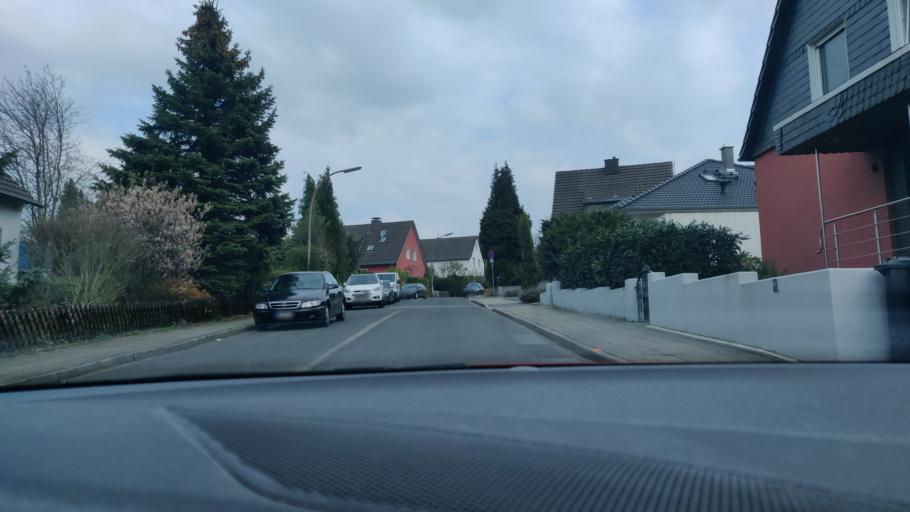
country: DE
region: North Rhine-Westphalia
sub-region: Regierungsbezirk Dusseldorf
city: Velbert
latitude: 51.3261
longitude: 7.0450
